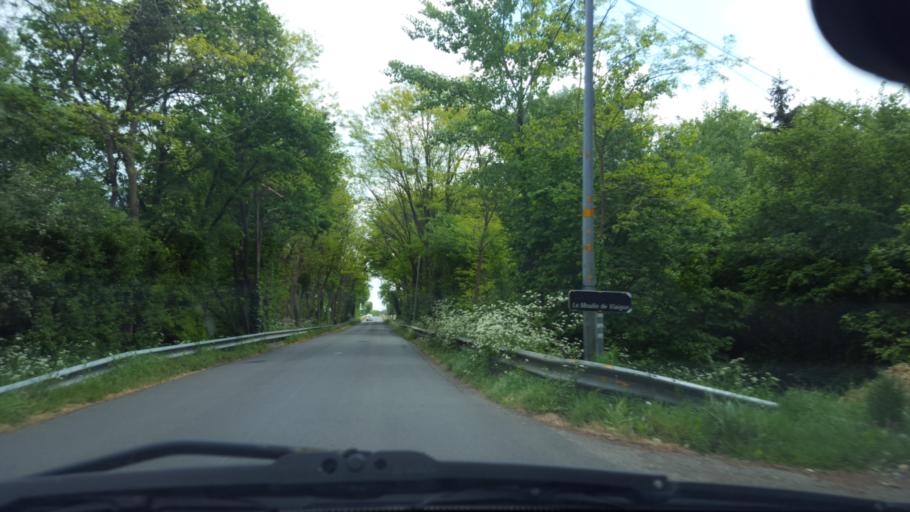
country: FR
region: Pays de la Loire
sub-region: Departement de la Loire-Atlantique
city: Saint-Philbert-de-Grand-Lieu
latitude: 47.0404
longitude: -1.6039
